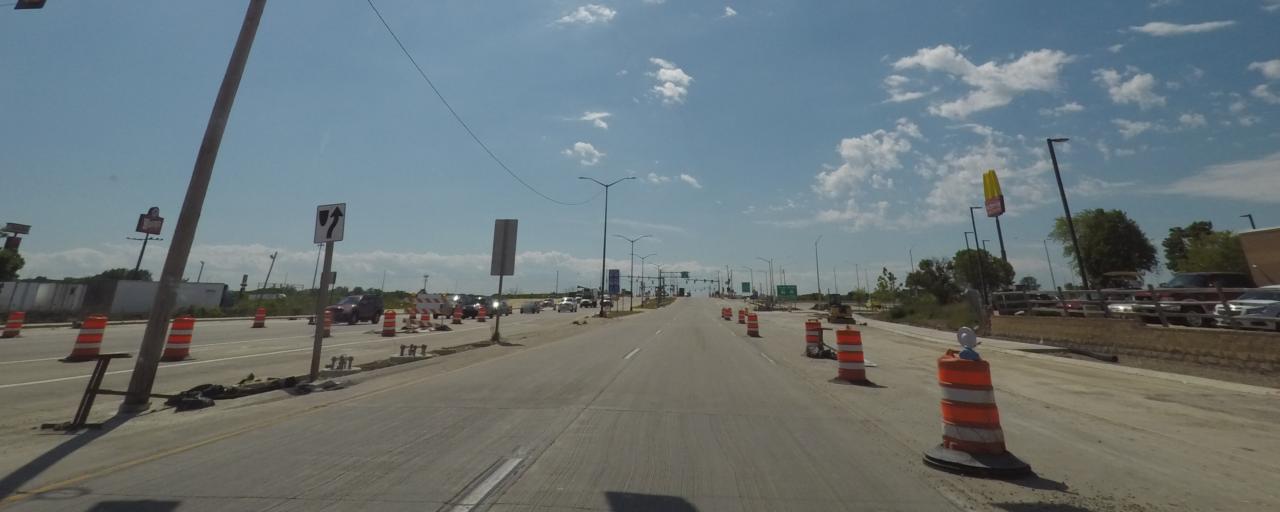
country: US
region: Wisconsin
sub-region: Racine County
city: Caledonia
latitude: 42.8725
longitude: -87.9327
